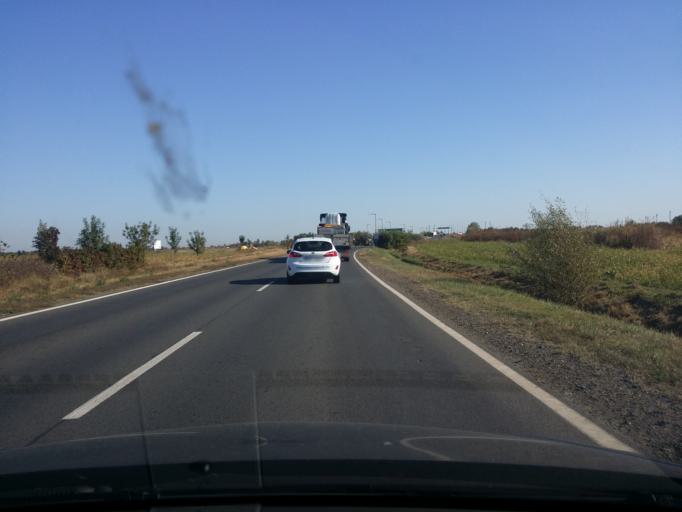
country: HU
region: Bekes
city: Bekescsaba
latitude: 46.6921
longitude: 21.0546
